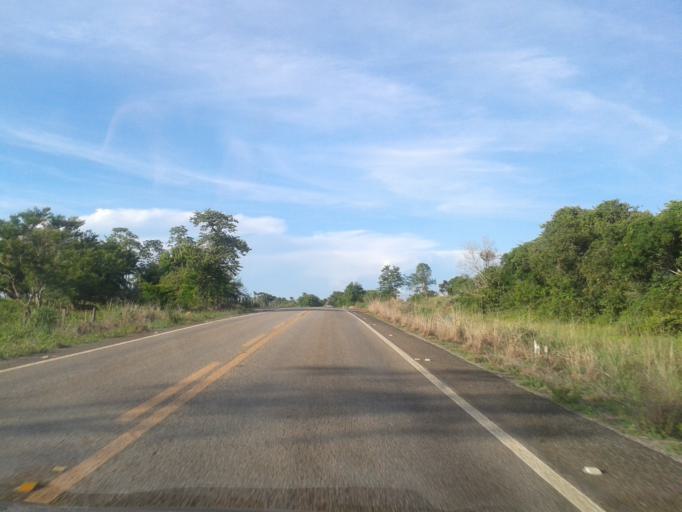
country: BR
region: Goias
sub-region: Sao Miguel Do Araguaia
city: Sao Miguel do Araguaia
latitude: -13.5434
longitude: -50.3077
